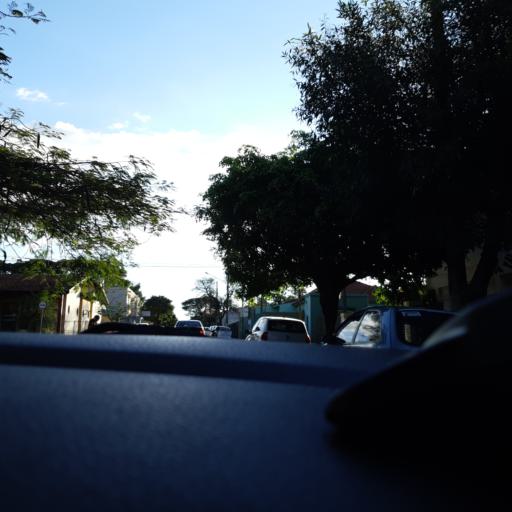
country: BR
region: Sao Paulo
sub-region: Ourinhos
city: Ourinhos
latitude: -22.9827
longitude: -49.8640
